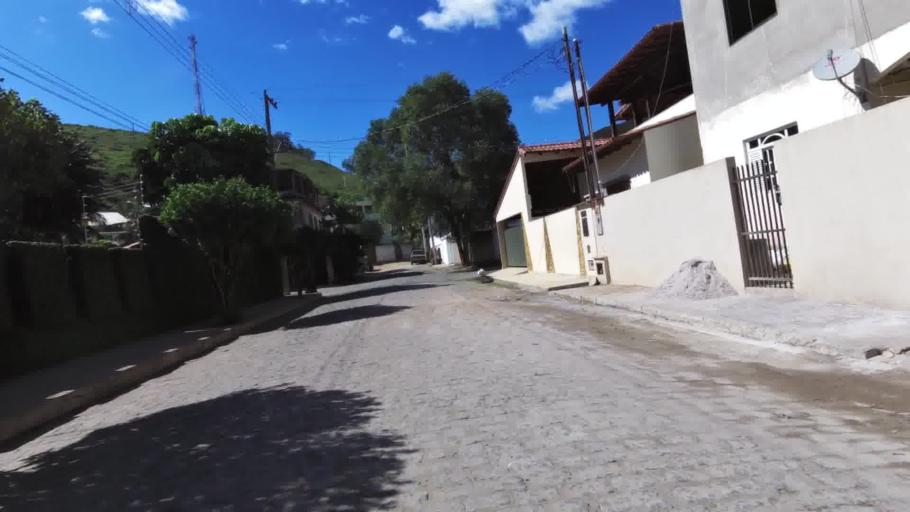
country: BR
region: Espirito Santo
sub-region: Rio Novo Do Sul
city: Rio Novo do Sul
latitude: -20.8638
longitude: -40.9301
